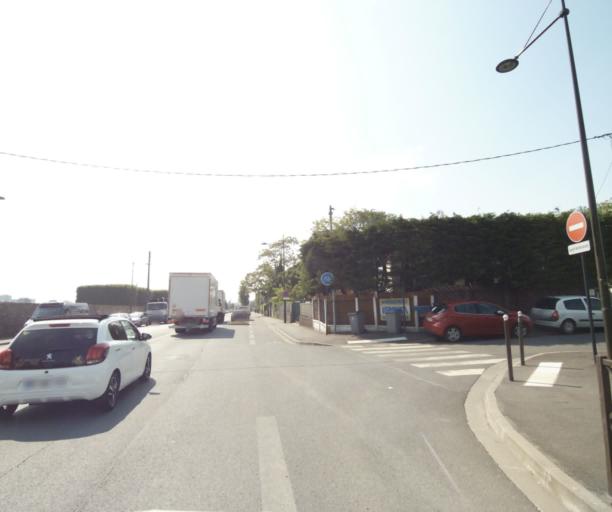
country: FR
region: Ile-de-France
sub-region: Departement du Val-d'Oise
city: Argenteuil
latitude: 48.9456
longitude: 2.2391
